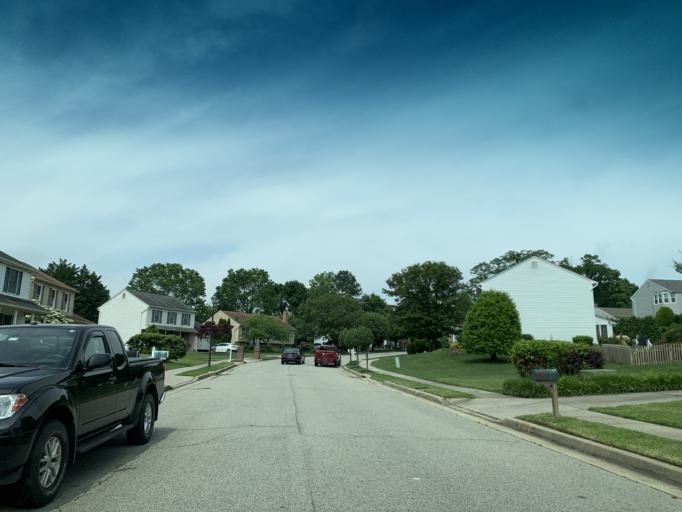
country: US
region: Maryland
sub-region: Baltimore County
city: Perry Hall
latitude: 39.4034
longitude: -76.4668
